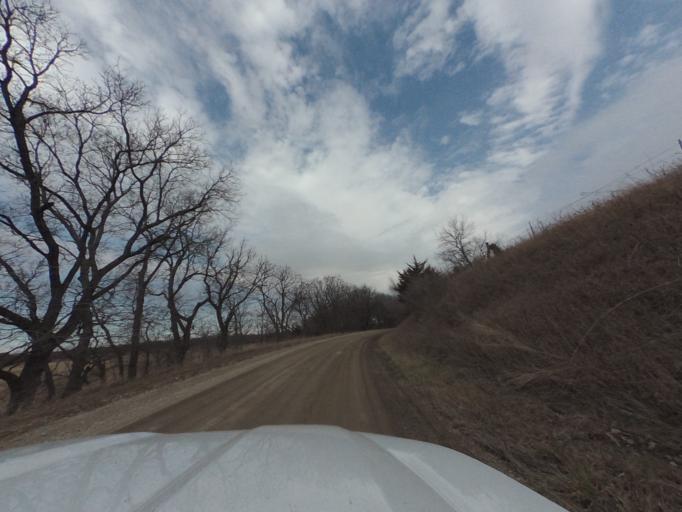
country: US
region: Kansas
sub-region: Chase County
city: Cottonwood Falls
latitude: 38.2804
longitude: -96.7350
